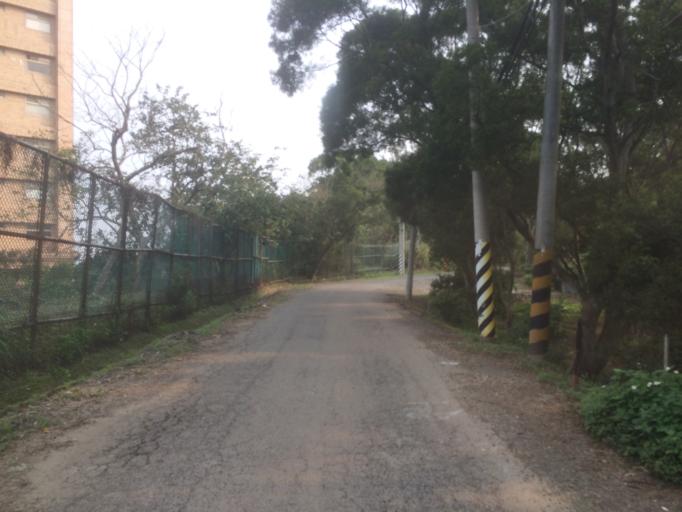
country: TW
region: Taiwan
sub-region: Hsinchu
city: Hsinchu
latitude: 24.7639
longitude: 120.9693
